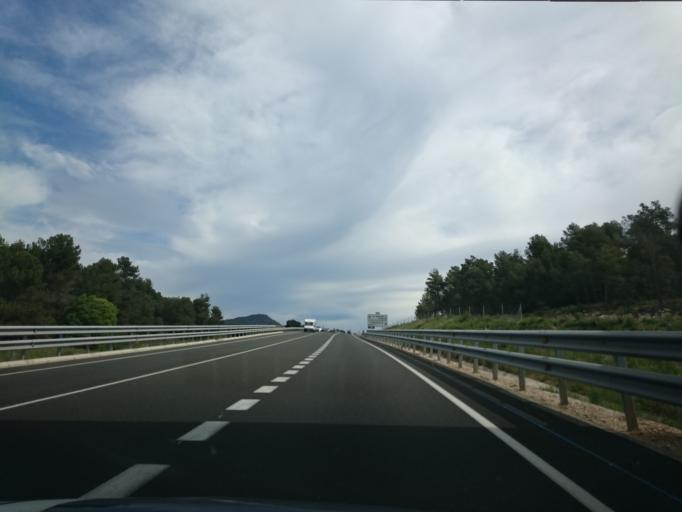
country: ES
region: Catalonia
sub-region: Provincia de Barcelona
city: Castelloli
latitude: 41.6204
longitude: 1.6833
